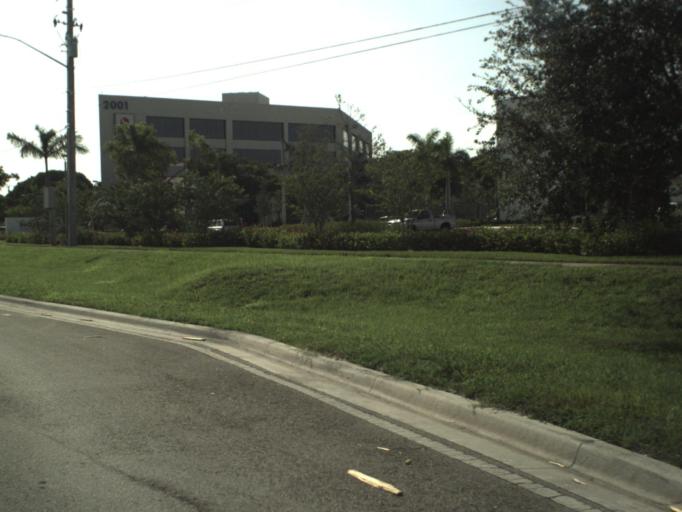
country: US
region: Florida
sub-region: Broward County
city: Tedder
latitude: 26.2747
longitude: -80.1492
